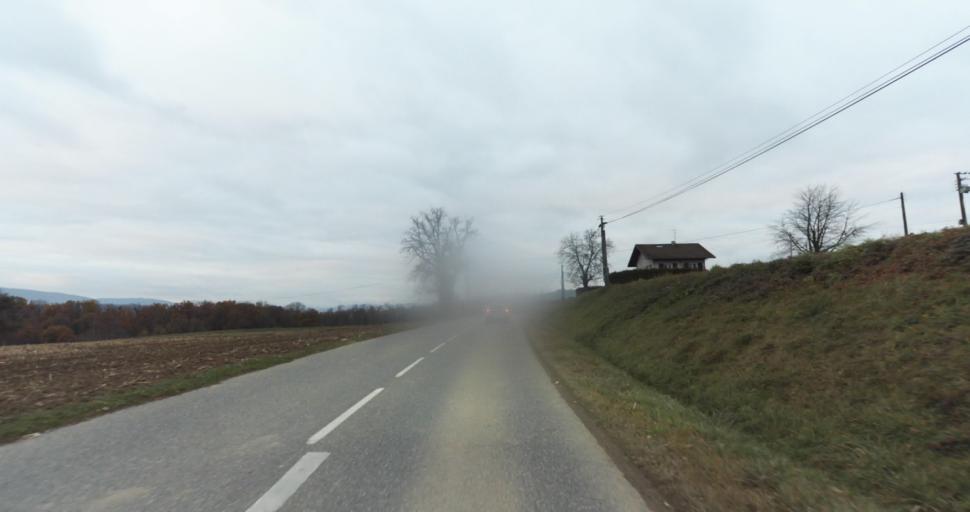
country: FR
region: Rhone-Alpes
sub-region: Departement de la Haute-Savoie
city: Saint-Felix
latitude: 45.8137
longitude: 5.9730
